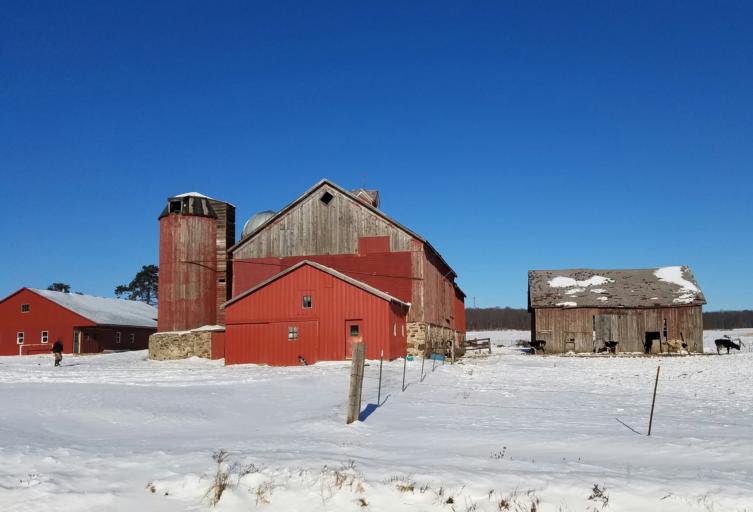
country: US
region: Wisconsin
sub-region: Clark County
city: Neillsville
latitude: 44.5674
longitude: -90.4452
